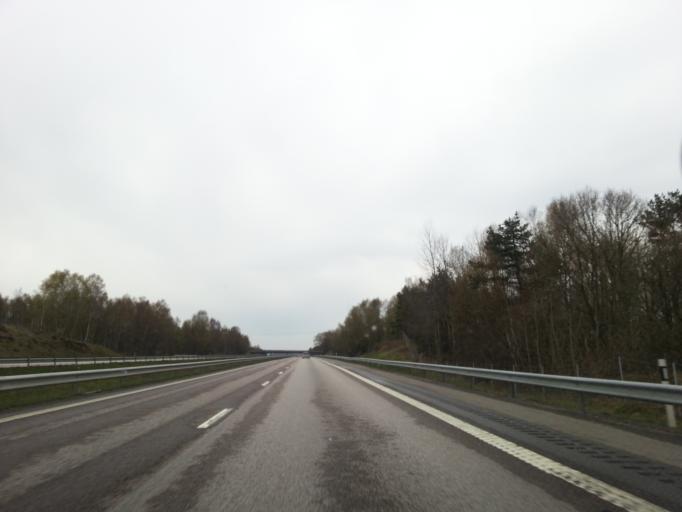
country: SE
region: Halland
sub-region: Kungsbacka Kommun
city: Frillesas
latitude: 57.2758
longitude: 12.2150
